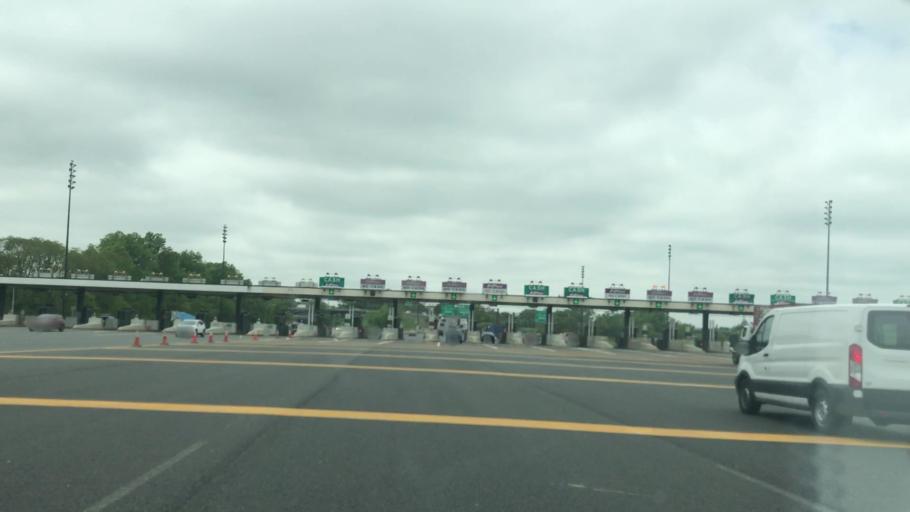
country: US
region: New Jersey
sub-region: Middlesex County
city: Fords
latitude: 40.5402
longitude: -74.2987
